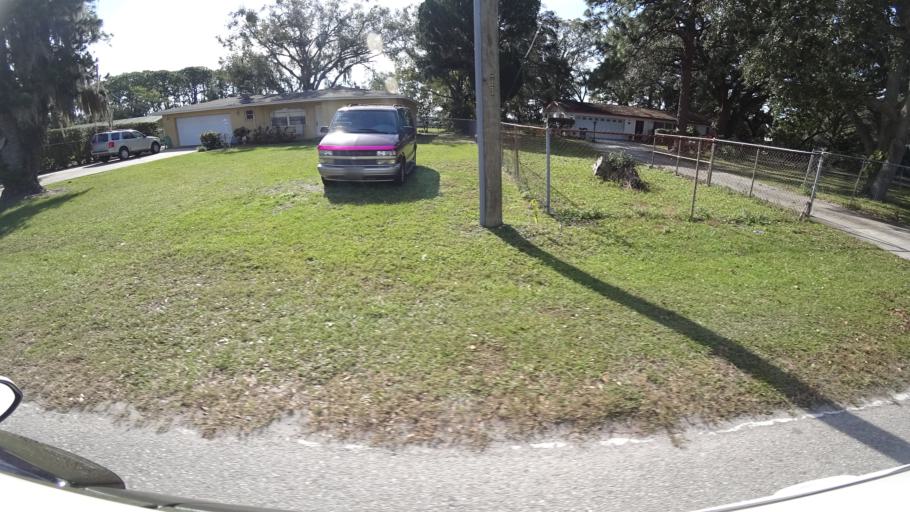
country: US
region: Florida
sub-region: Manatee County
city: Whitfield
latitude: 27.4329
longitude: -82.5608
